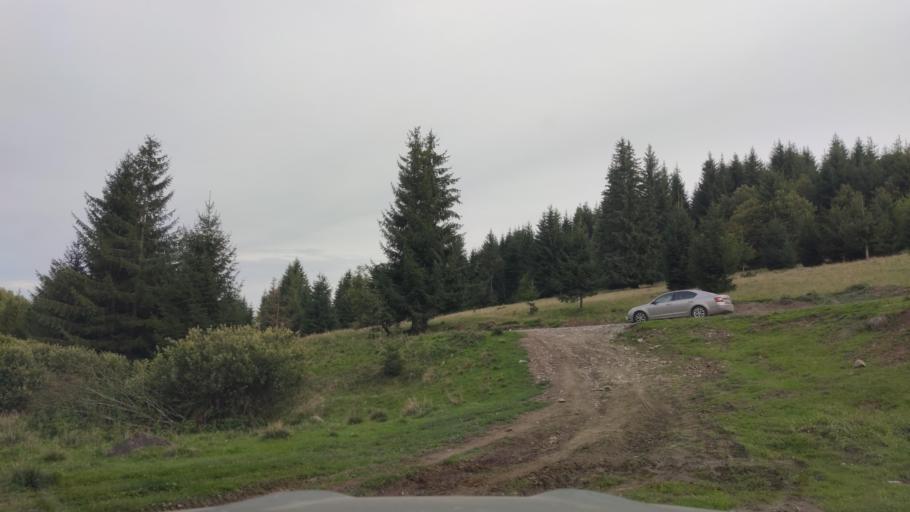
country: RO
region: Harghita
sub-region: Comuna Remetea
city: Remetea
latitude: 46.8144
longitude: 25.3556
